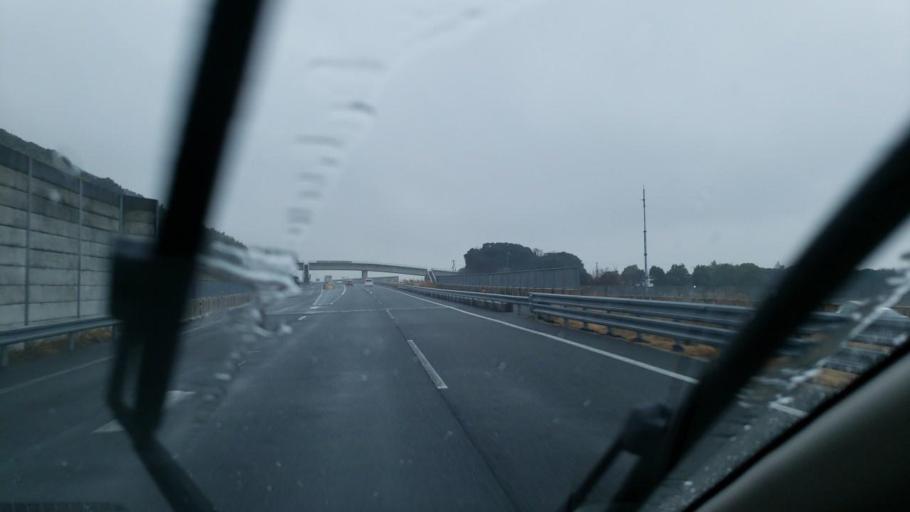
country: JP
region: Hyogo
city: Akashi
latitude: 34.5437
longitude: 134.9806
